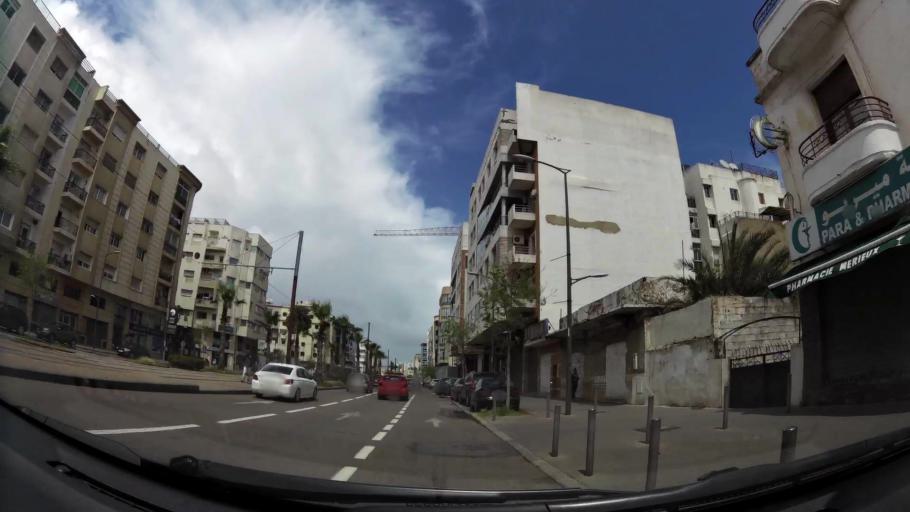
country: MA
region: Grand Casablanca
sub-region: Casablanca
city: Casablanca
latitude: 33.5672
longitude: -7.6262
